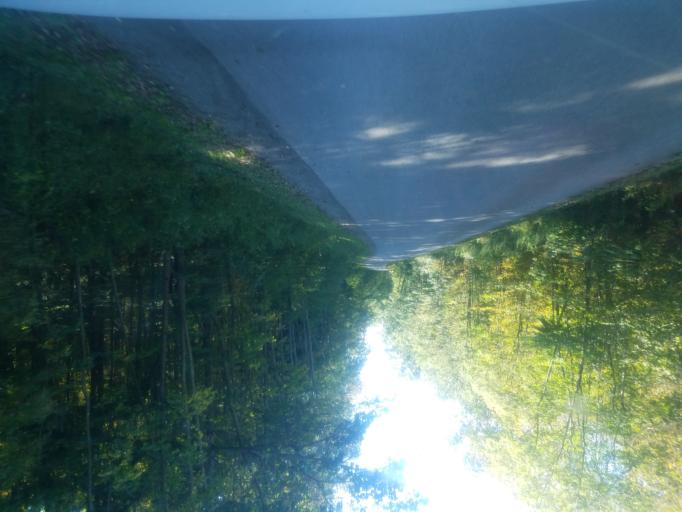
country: US
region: New York
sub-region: Allegany County
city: Cuba
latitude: 42.3124
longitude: -78.2051
